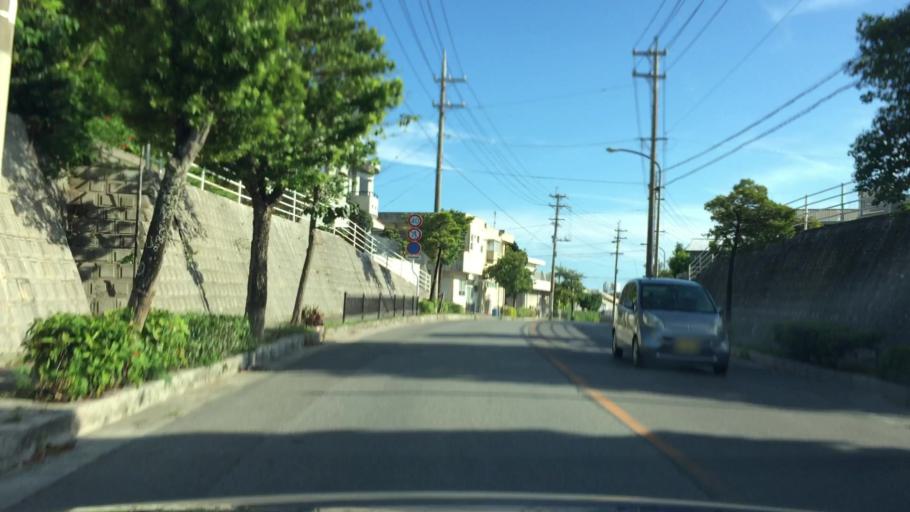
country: JP
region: Okinawa
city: Ishigaki
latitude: 24.3472
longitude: 124.1577
